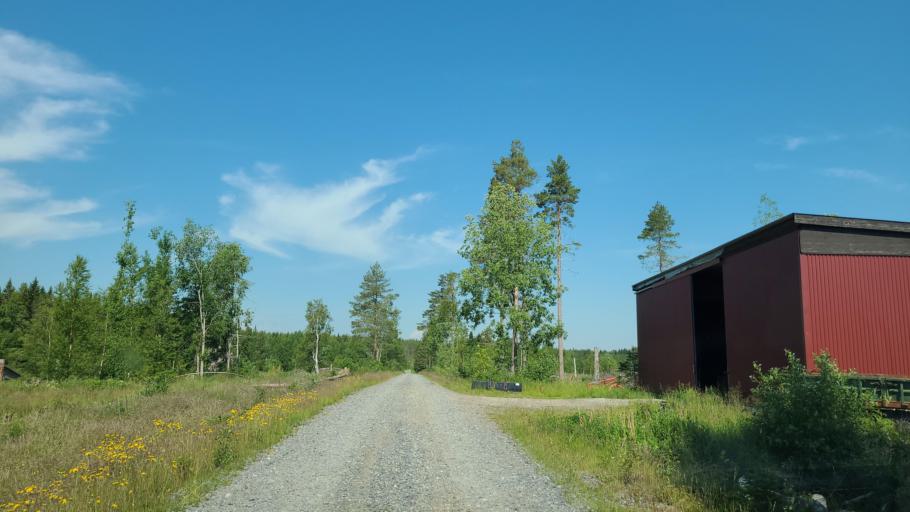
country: SE
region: Vaesterbotten
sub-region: Robertsfors Kommun
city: Robertsfors
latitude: 64.0877
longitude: 20.8399
